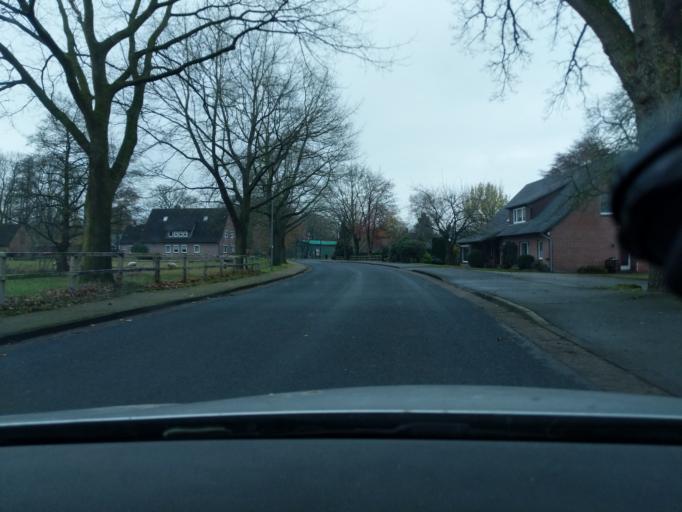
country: DE
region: Lower Saxony
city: Klein Meckelsen
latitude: 53.3487
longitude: 9.4002
